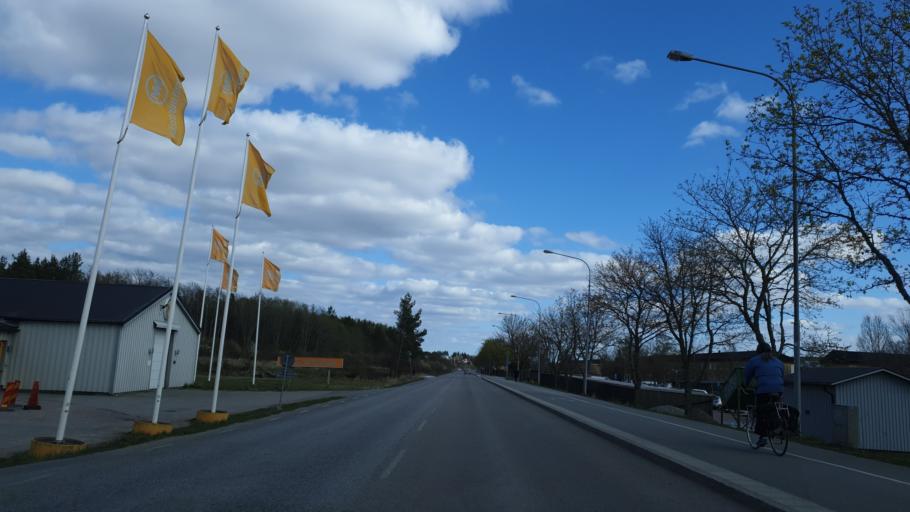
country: SE
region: Uppsala
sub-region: Uppsala Kommun
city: Gamla Uppsala
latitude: 59.8907
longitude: 17.6526
